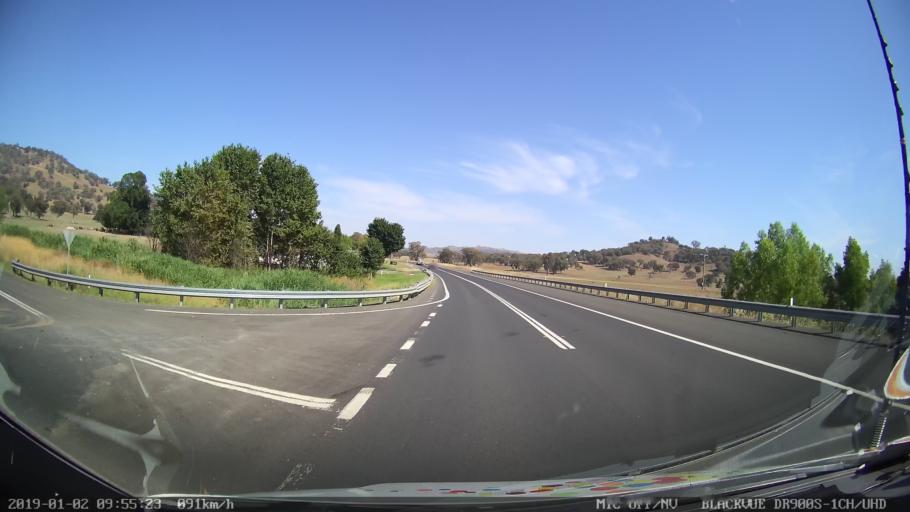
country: AU
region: New South Wales
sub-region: Tumut Shire
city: Tumut
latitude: -35.2240
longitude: 148.1891
